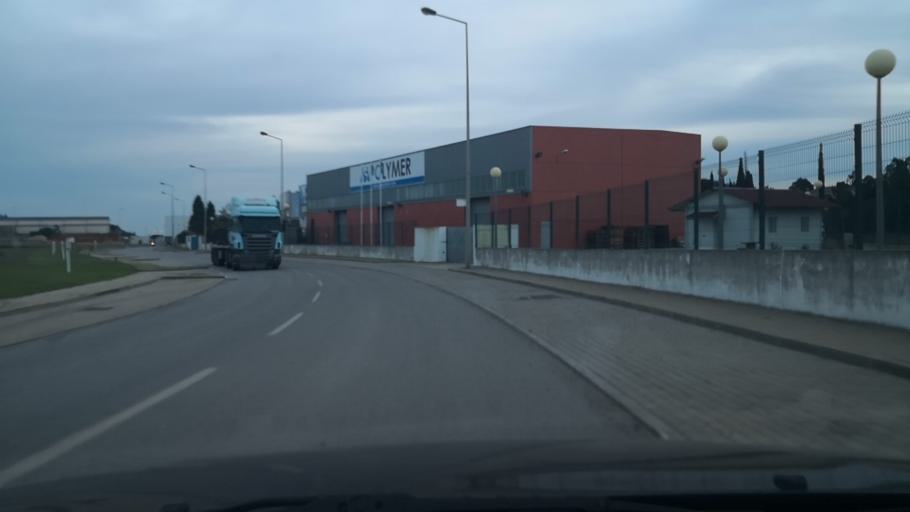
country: PT
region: Setubal
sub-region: Setubal
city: Setubal
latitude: 38.4977
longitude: -8.8294
